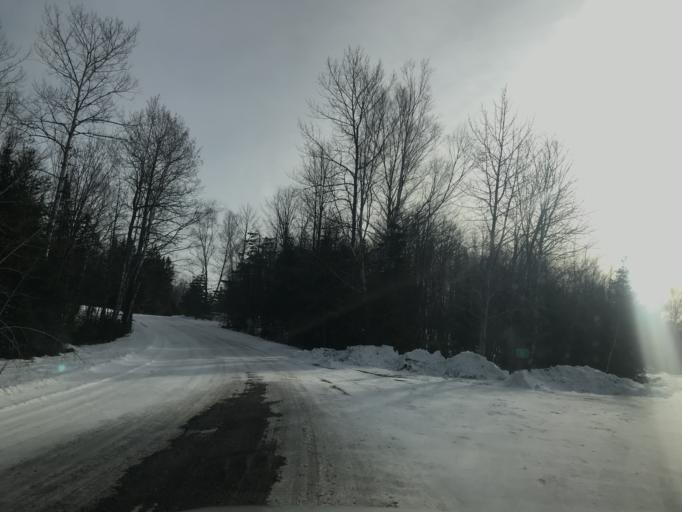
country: US
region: Wisconsin
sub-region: Door County
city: Sturgeon Bay
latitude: 45.1520
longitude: -87.0548
